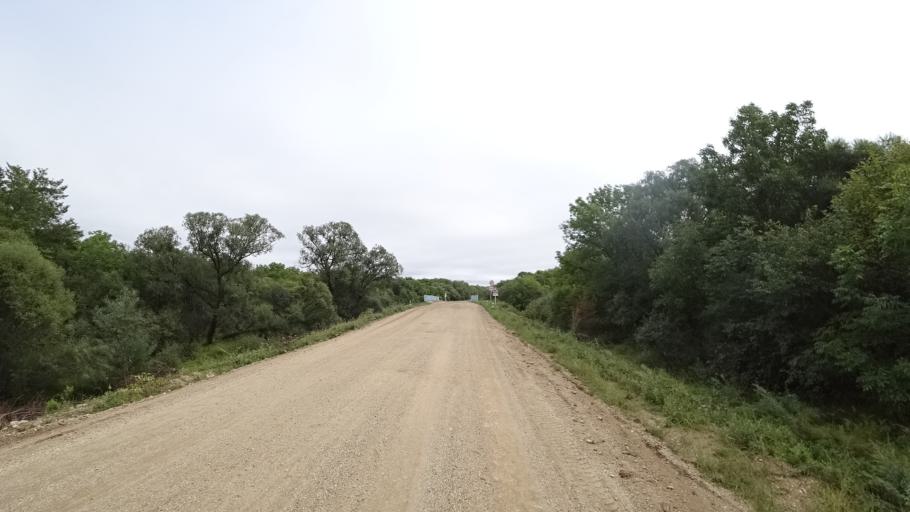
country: RU
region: Primorskiy
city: Lyalichi
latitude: 44.0827
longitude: 132.4472
